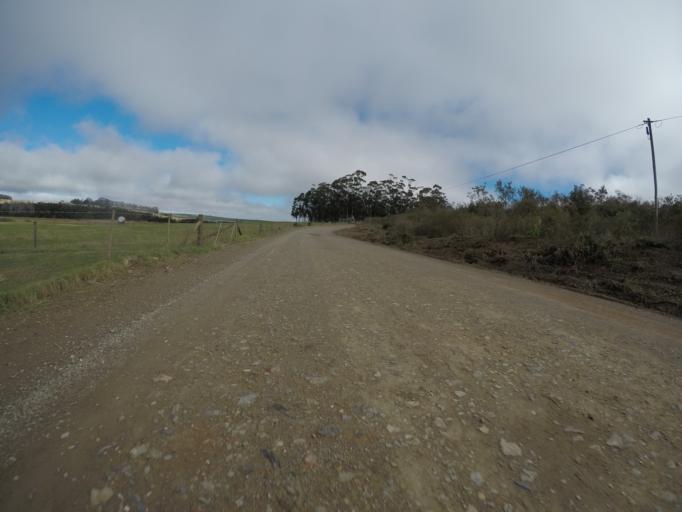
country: ZA
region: Western Cape
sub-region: Cape Winelands District Municipality
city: Ashton
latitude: -34.1260
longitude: 19.8236
